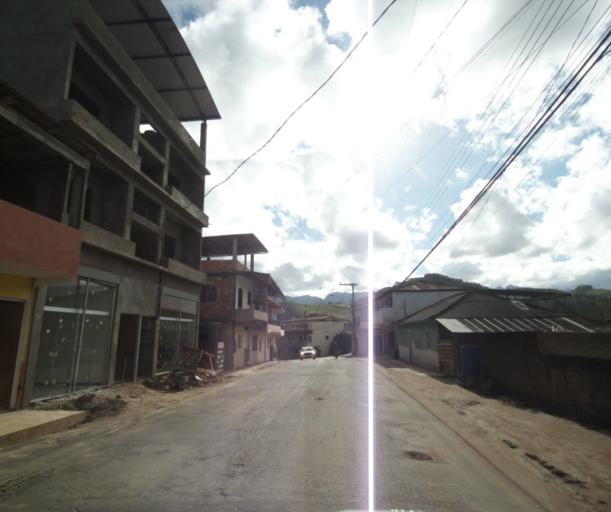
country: BR
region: Espirito Santo
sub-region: Irupi
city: Irupi
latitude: -20.5399
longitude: -41.6624
